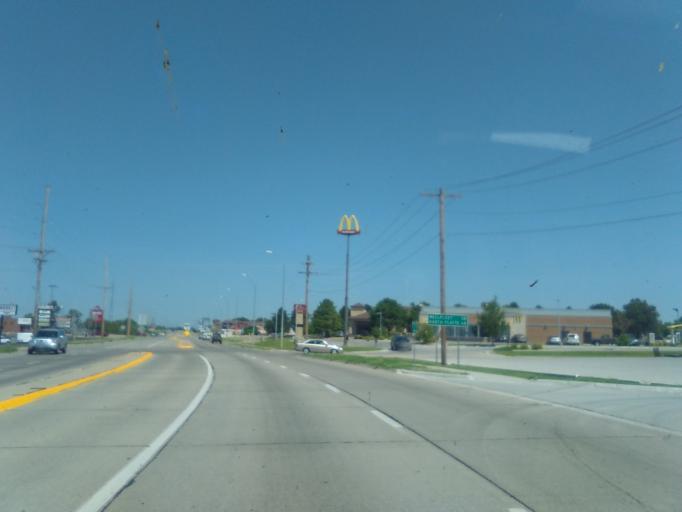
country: US
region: Nebraska
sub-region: Red Willow County
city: McCook
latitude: 40.2009
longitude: -100.6443
